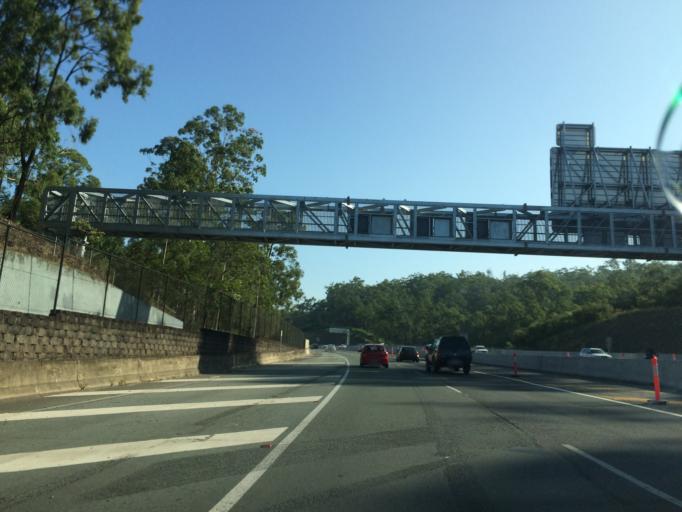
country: AU
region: Queensland
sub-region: Brisbane
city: Taringa
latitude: -27.4836
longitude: 152.9683
